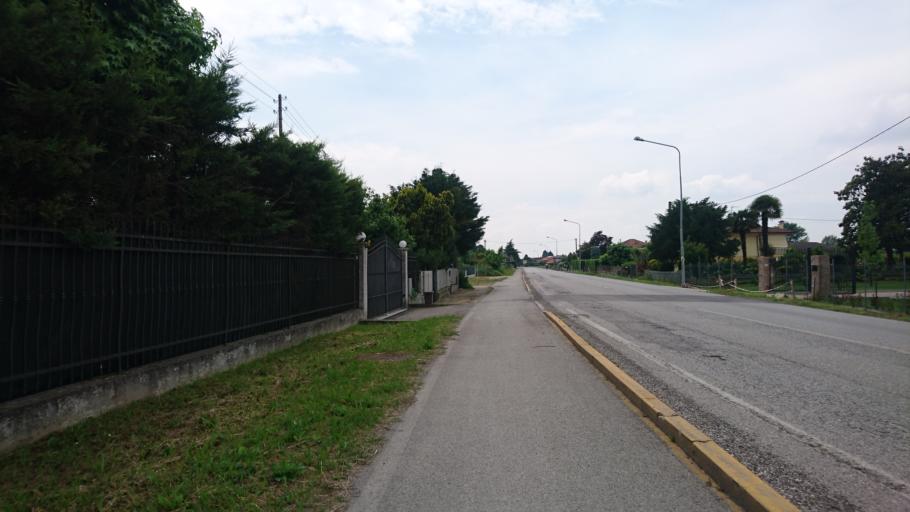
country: IT
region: Veneto
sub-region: Provincia di Rovigo
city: Badia Polesine
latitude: 45.0888
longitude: 11.4790
